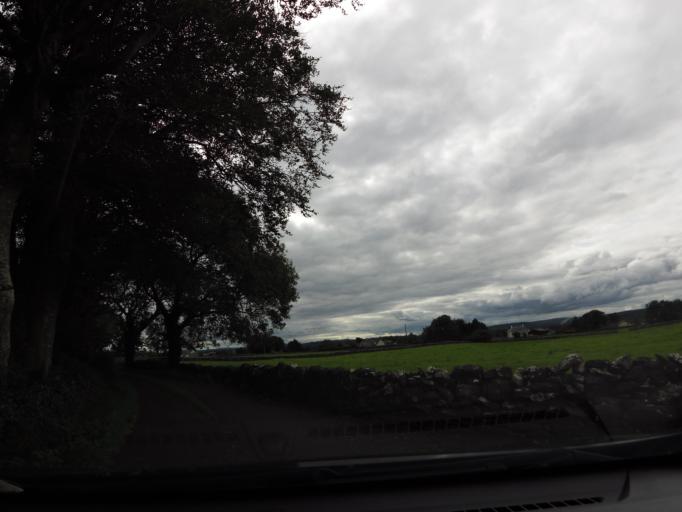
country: IE
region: Connaught
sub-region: County Galway
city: Loughrea
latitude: 53.1503
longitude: -8.4173
